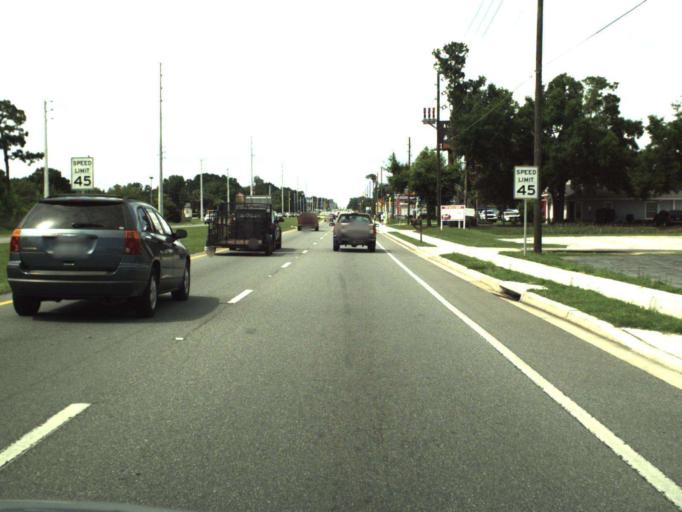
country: US
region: Florida
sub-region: Marion County
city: Silver Springs Shores
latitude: 29.1608
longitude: -82.0535
